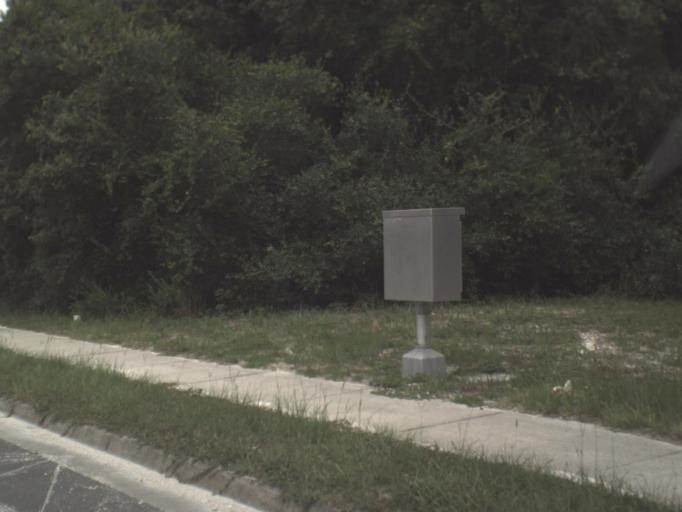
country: US
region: Florida
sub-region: Citrus County
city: Inverness
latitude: 28.8495
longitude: -82.2677
